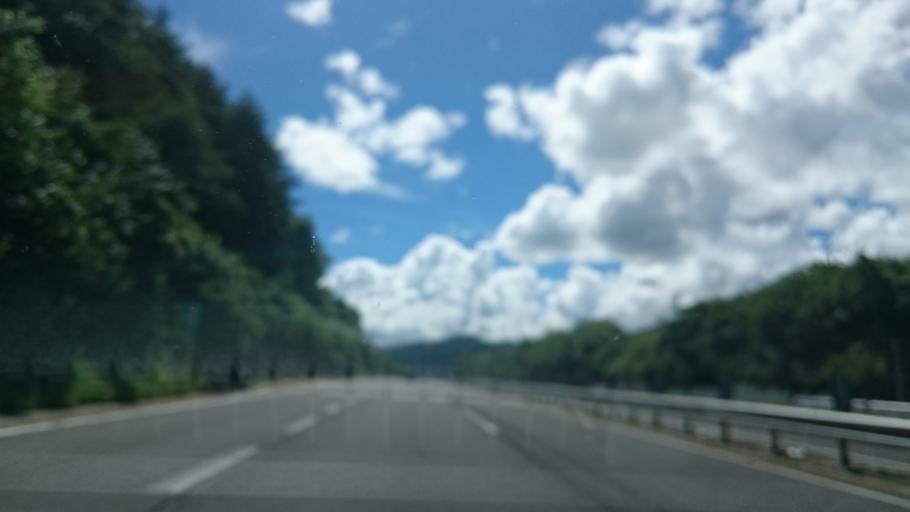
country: JP
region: Nagano
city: Iida
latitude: 35.4842
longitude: 137.7732
